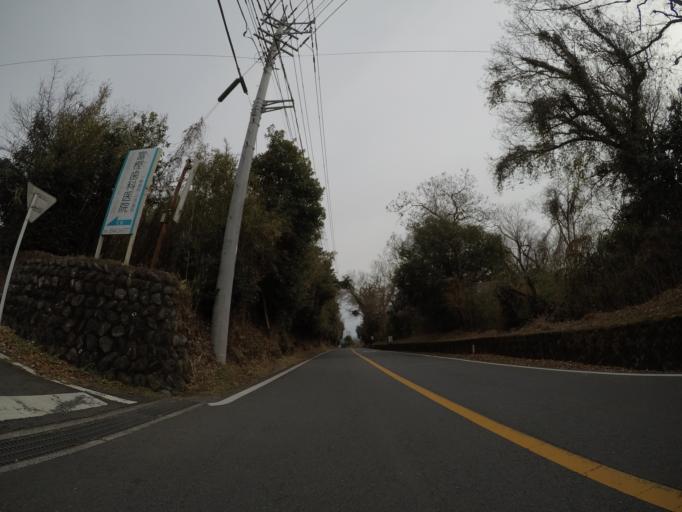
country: JP
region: Shizuoka
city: Fujinomiya
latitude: 35.2152
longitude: 138.6639
